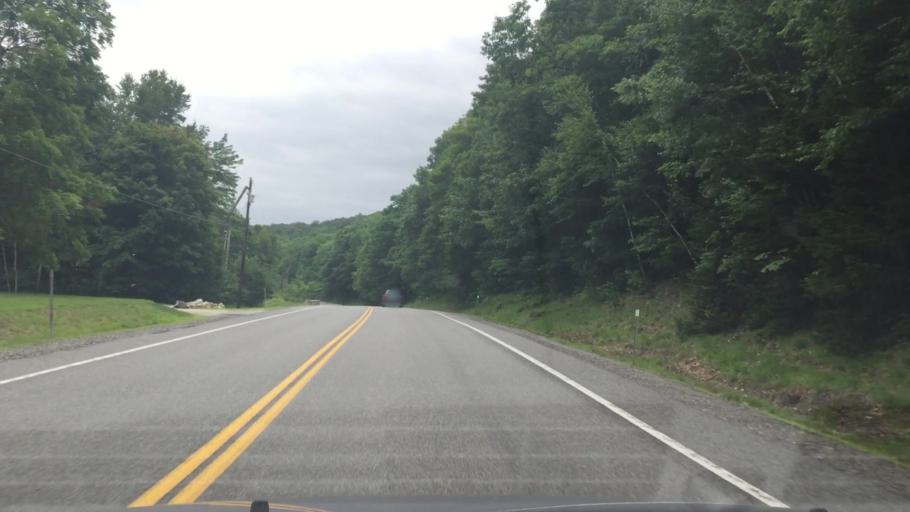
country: US
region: New Hampshire
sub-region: Carroll County
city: North Conway
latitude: 44.1287
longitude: -71.3601
